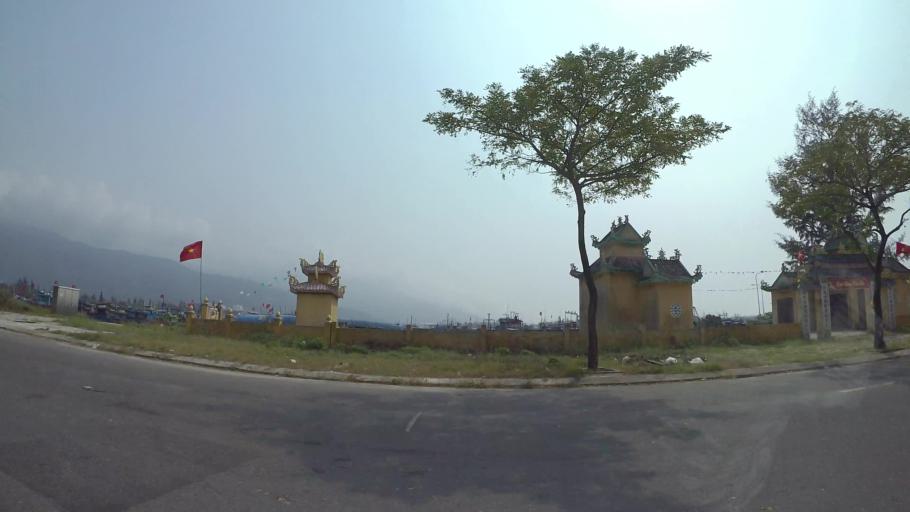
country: VN
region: Da Nang
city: Da Nang
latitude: 16.1001
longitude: 108.2349
